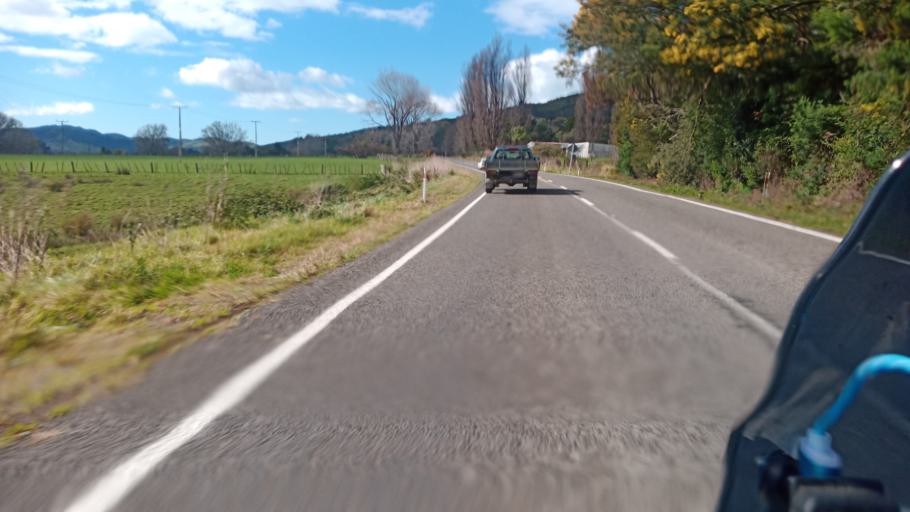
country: NZ
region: Gisborne
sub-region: Gisborne District
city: Gisborne
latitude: -37.9071
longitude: 178.2870
